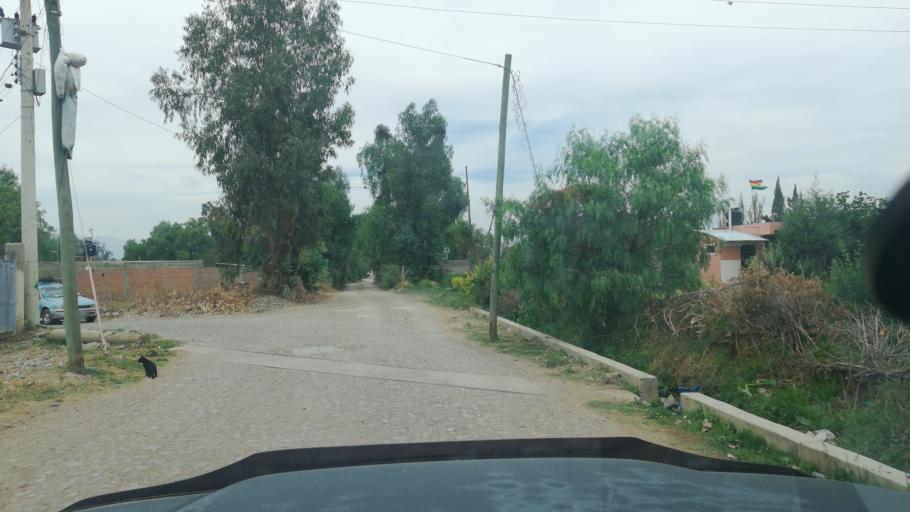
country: BO
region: Cochabamba
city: Cochabamba
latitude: -17.3585
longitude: -66.2214
